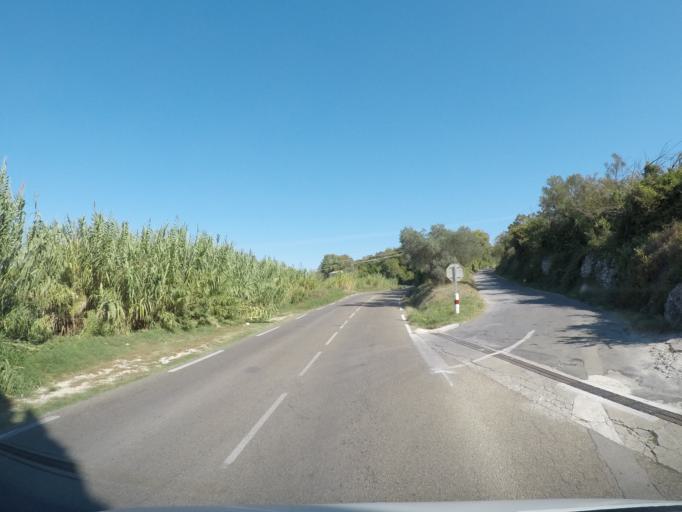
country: FR
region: Languedoc-Roussillon
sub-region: Departement du Gard
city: Uzes
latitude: 44.0057
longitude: 4.4043
